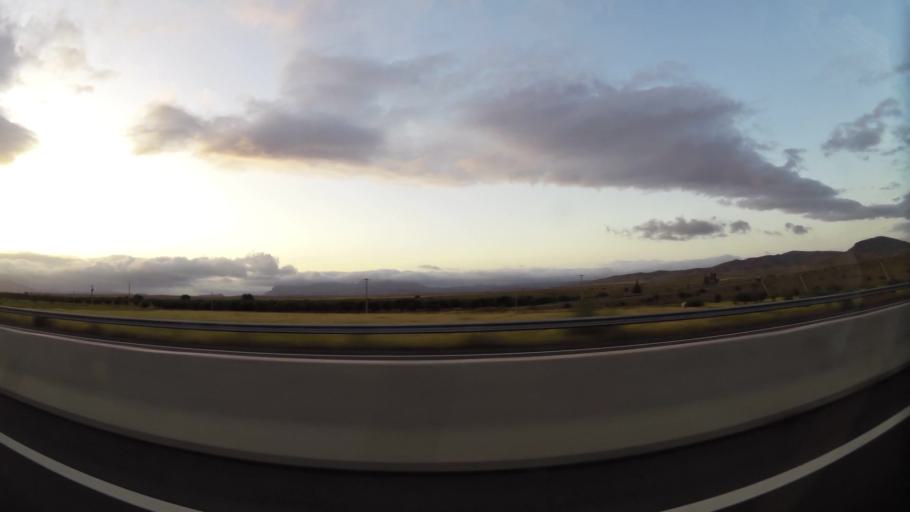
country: MA
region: Oriental
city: El Aioun
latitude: 34.5937
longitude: -2.6967
